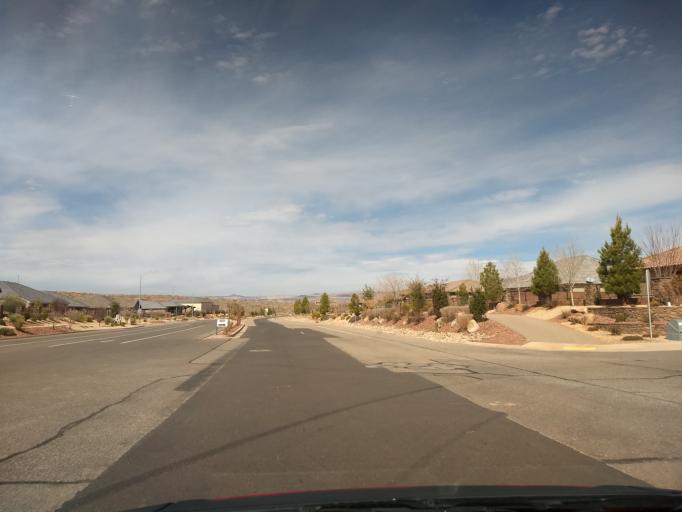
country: US
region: Utah
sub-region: Washington County
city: Washington
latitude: 37.0675
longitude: -113.4922
